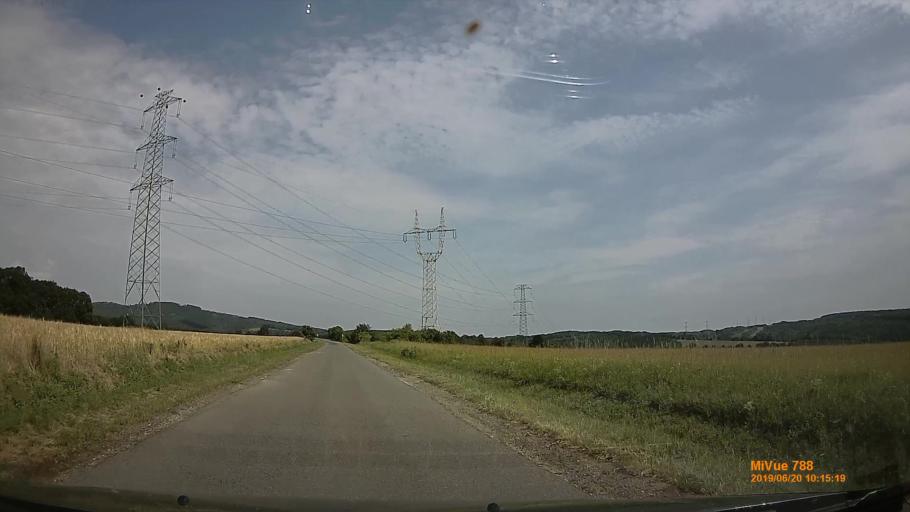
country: HU
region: Baranya
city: Mecseknadasd
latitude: 46.1908
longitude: 18.4653
